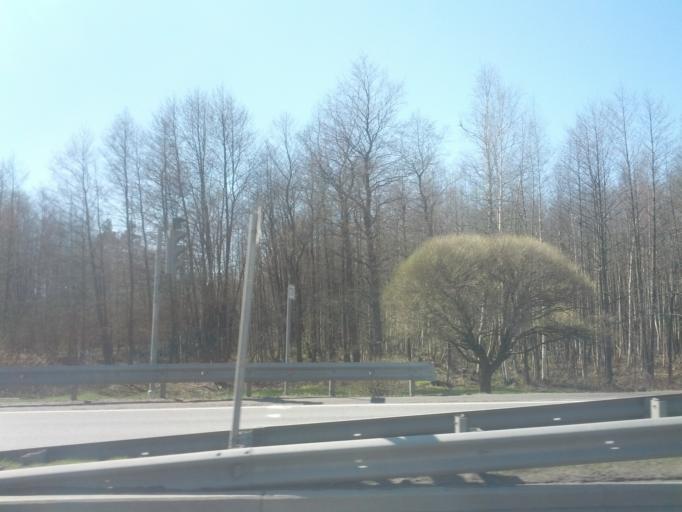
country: RU
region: St.-Petersburg
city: Razliv
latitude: 60.0761
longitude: 29.9642
